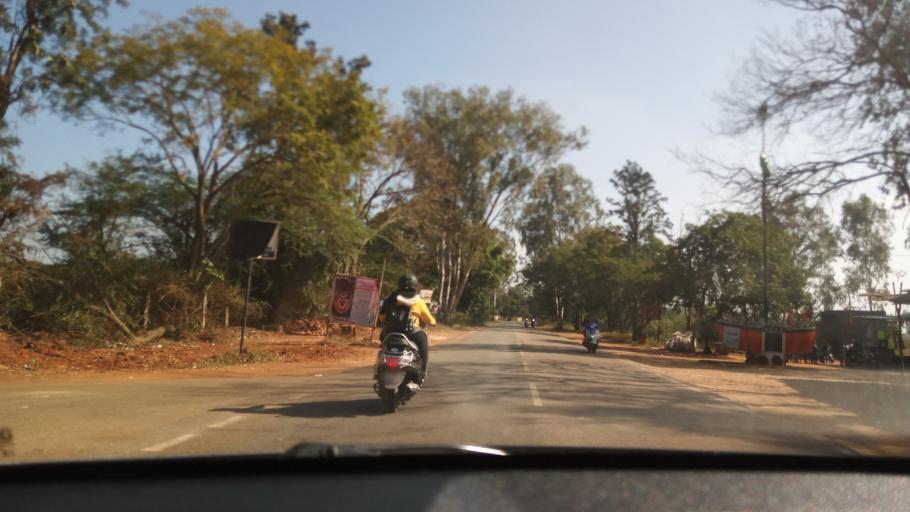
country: IN
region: Karnataka
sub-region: Bangalore Rural
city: Vijayapura
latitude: 13.2873
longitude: 77.7743
